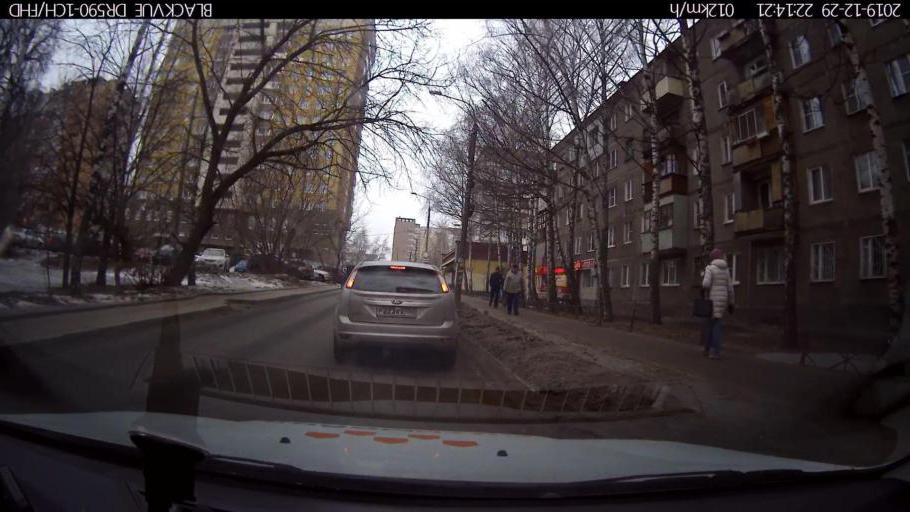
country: RU
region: Nizjnij Novgorod
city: Nizhniy Novgorod
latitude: 56.2323
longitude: 43.9527
